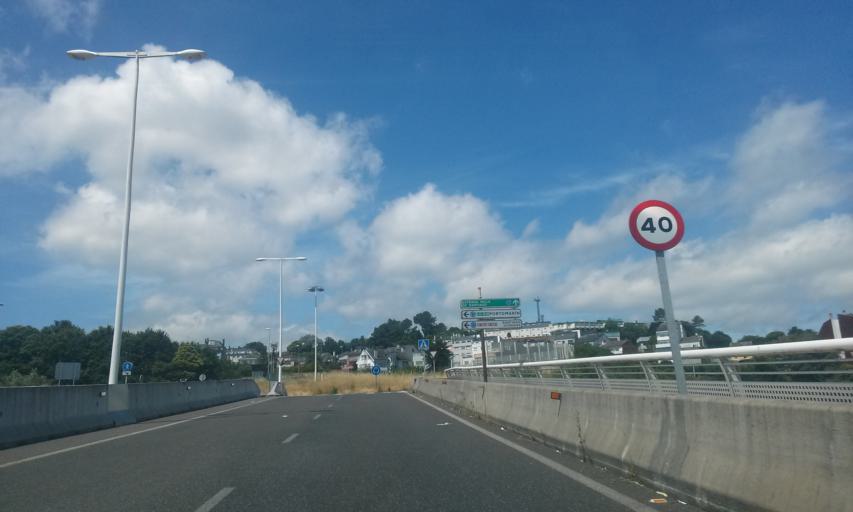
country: ES
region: Galicia
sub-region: Provincia de Lugo
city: Lugo
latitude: 42.9964
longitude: -7.5624
